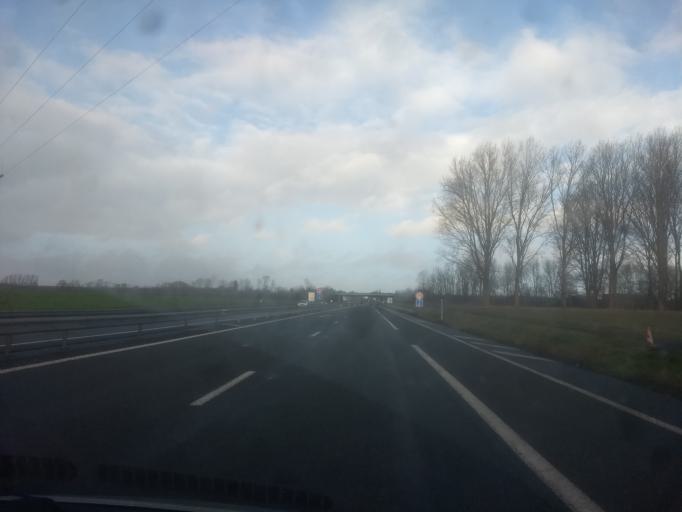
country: FR
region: Nord-Pas-de-Calais
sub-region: Departement du Pas-de-Calais
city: Thelus
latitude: 50.3473
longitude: 2.7855
